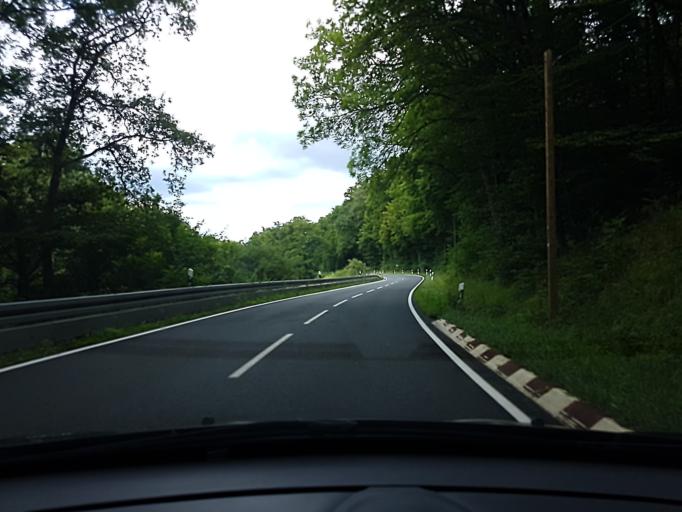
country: DE
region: Hesse
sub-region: Regierungsbezirk Giessen
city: Laubach
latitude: 50.5322
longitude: 9.0496
